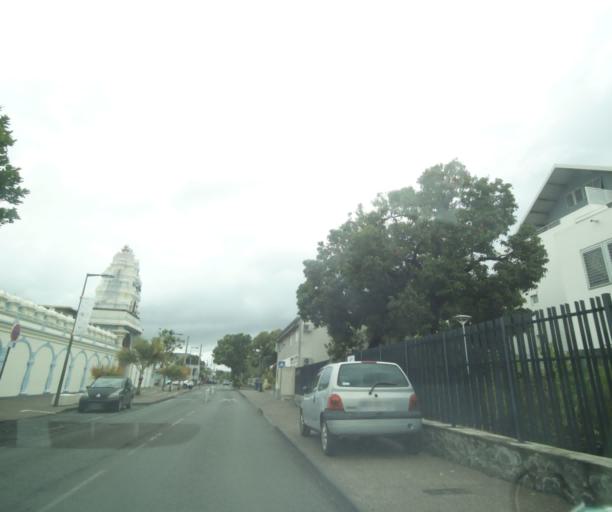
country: RE
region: Reunion
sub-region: Reunion
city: Saint-Paul
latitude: -21.0047
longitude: 55.2782
